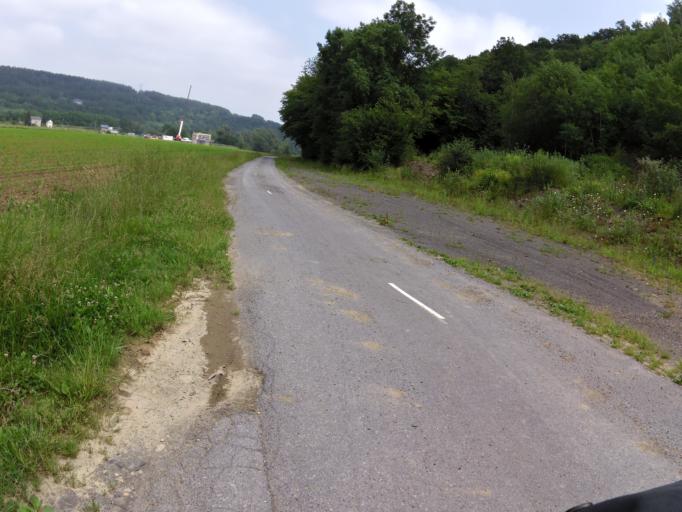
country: BE
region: Wallonia
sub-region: Province de Namur
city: Doische
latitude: 50.1084
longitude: 4.7708
